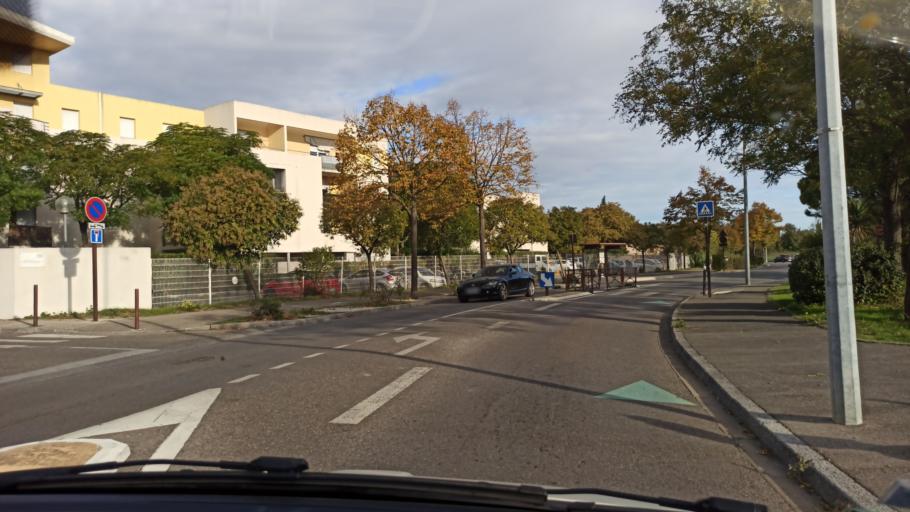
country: FR
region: Provence-Alpes-Cote d'Azur
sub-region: Departement du Vaucluse
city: Le Pontet
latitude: 43.9459
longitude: 4.8522
